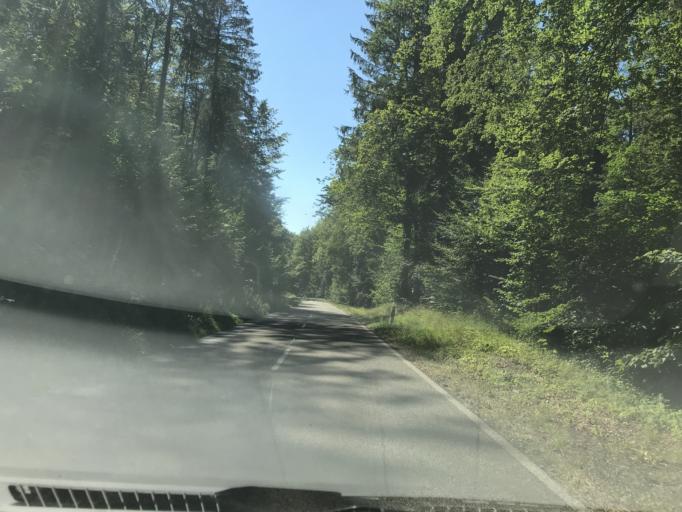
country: DE
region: Baden-Wuerttemberg
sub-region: Freiburg Region
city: Hausen
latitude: 47.6603
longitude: 7.8556
